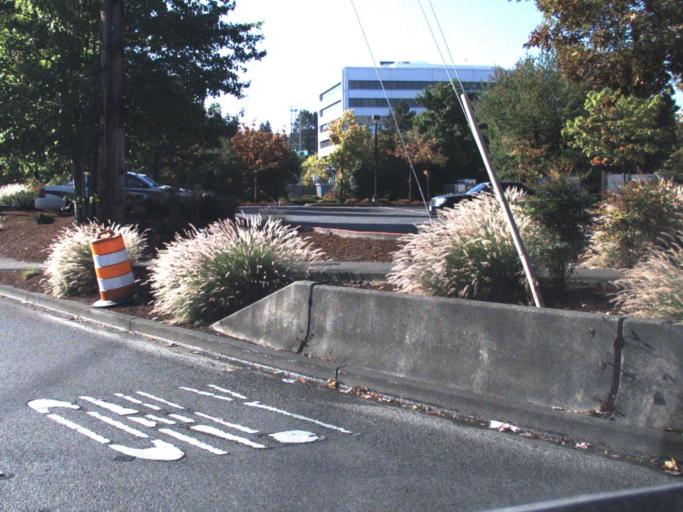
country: US
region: Washington
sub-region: King County
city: Renton
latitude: 47.4720
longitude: -122.2081
